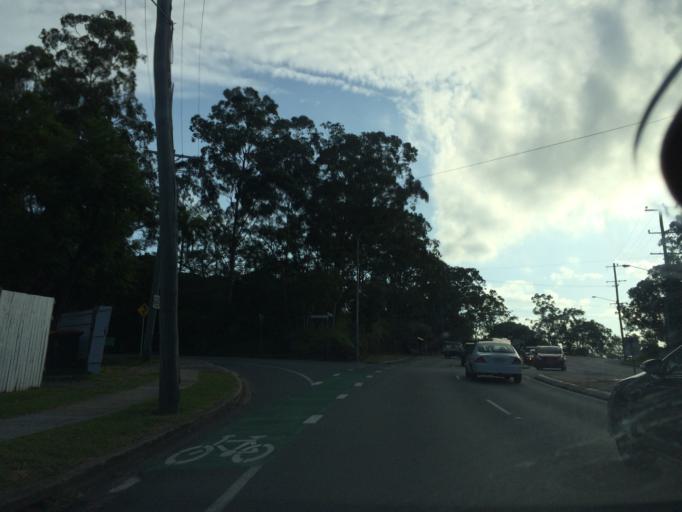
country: AU
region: Queensland
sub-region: Brisbane
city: Kenmore Hills
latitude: -27.5083
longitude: 152.9553
